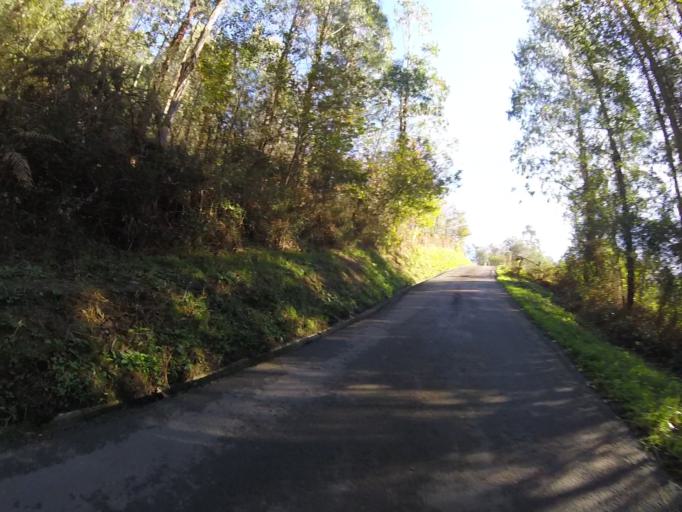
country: ES
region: Basque Country
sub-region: Provincia de Guipuzcoa
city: Usurbil
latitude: 43.2881
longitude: -2.0732
